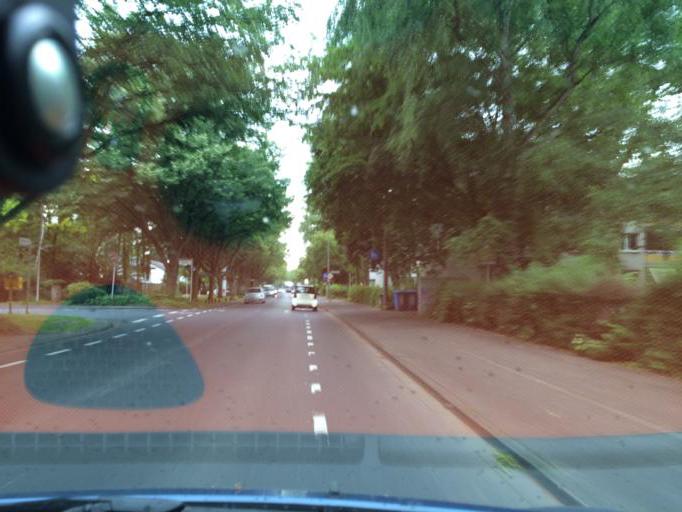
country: DE
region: North Rhine-Westphalia
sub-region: Regierungsbezirk Koln
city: Konigswinter
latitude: 50.7002
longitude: 7.1550
